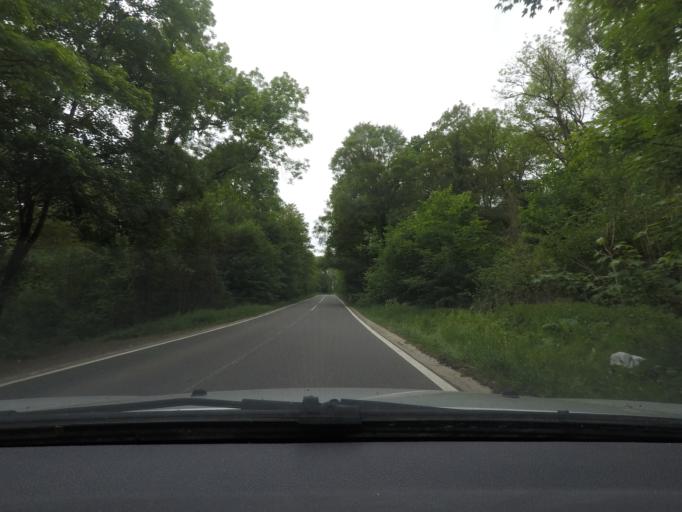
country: BE
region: Wallonia
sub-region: Province de Namur
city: Noville-les-Bois
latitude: 50.5148
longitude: 4.9891
